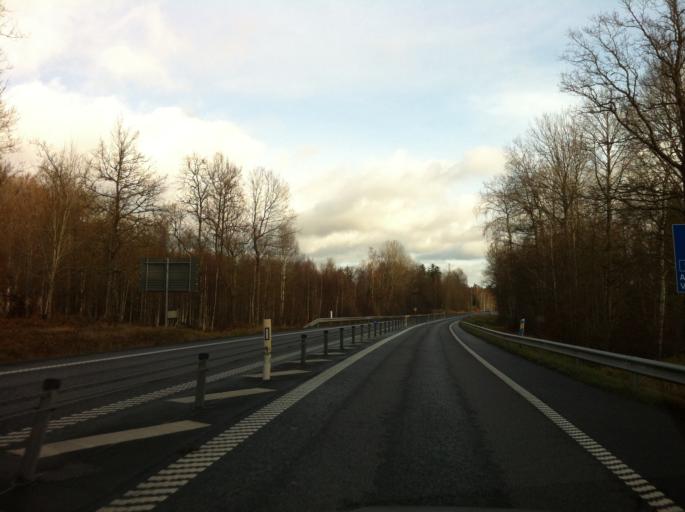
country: SE
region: Kronoberg
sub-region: Alvesta Kommun
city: Vislanda
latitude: 56.7034
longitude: 14.3893
